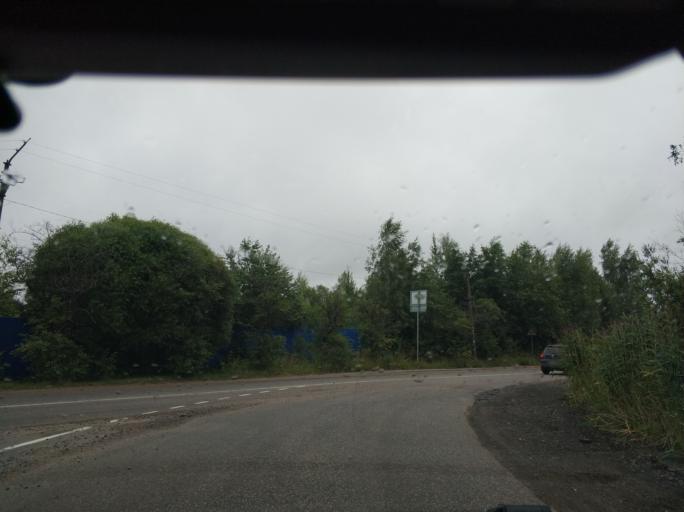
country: RU
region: Leningrad
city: Imeni Morozova
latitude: 59.9760
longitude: 31.0248
